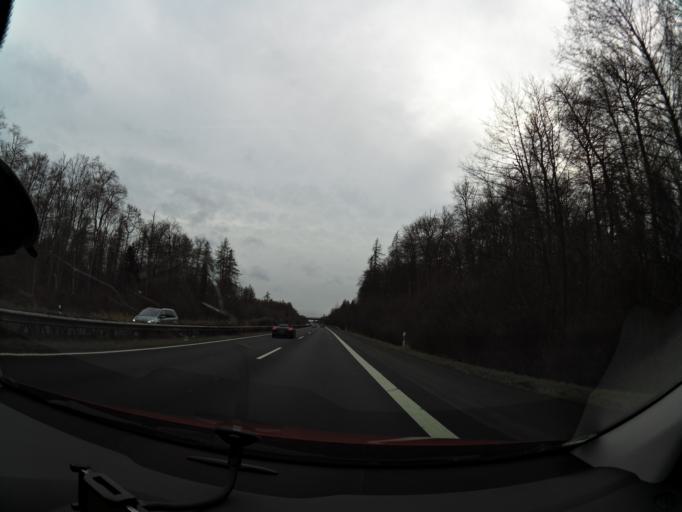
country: DE
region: Lower Saxony
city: Flothe
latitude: 52.1136
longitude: 10.4875
